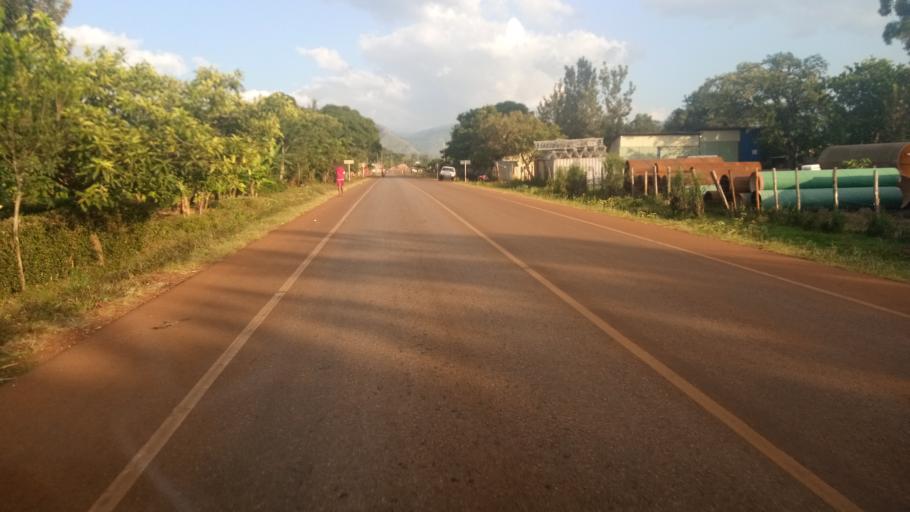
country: UG
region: Eastern Region
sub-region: Sironko District
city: Sironko
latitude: 1.3230
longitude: 34.3331
